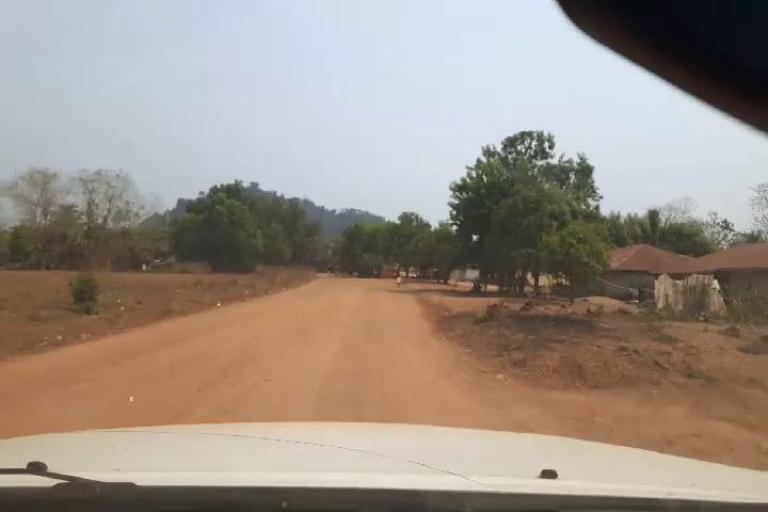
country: SL
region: Northern Province
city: Masingbi
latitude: 8.8646
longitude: -11.8180
